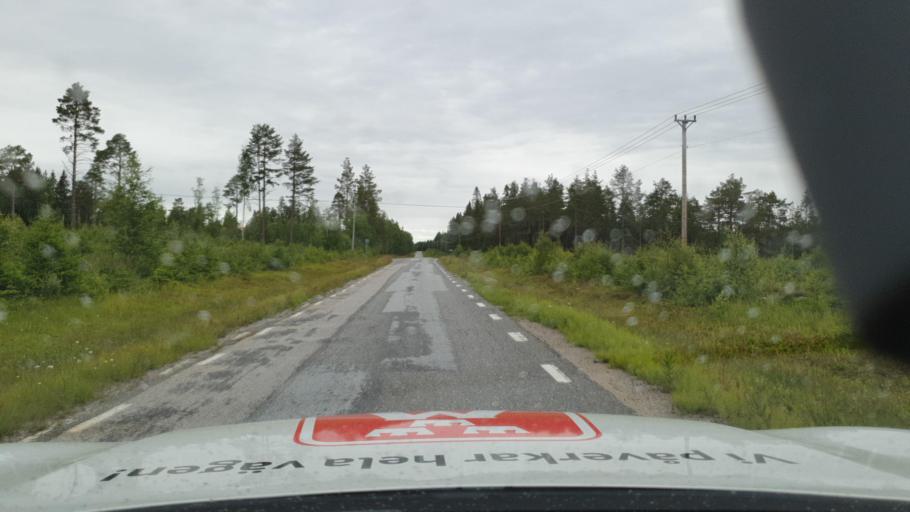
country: SE
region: Vaesterbotten
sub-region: Nordmalings Kommun
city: Nordmaling
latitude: 63.4524
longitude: 19.4676
